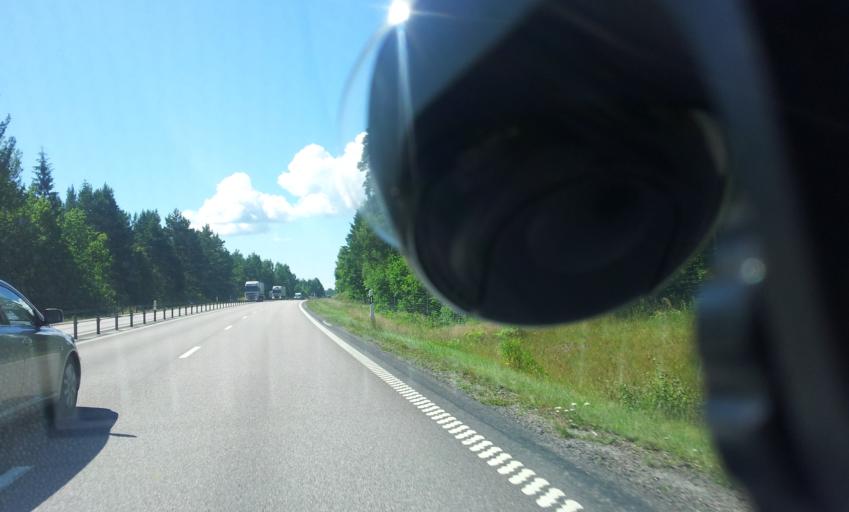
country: SE
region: Kalmar
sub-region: Oskarshamns Kommun
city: Paskallavik
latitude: 57.2058
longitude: 16.4372
